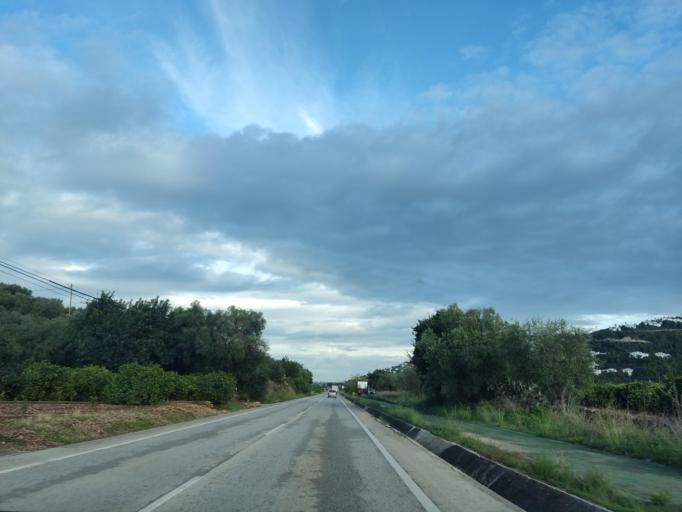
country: ES
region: Valencia
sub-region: Provincia de Alicante
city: Sagra
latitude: 38.8484
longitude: -0.0776
